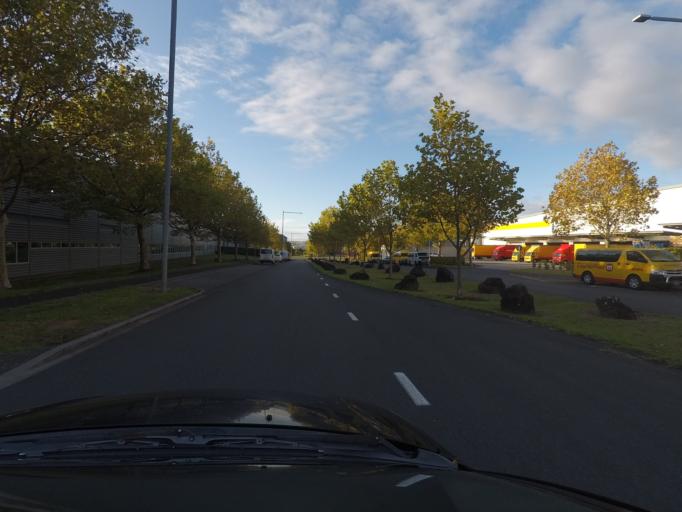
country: NZ
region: Auckland
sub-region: Auckland
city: Manukau City
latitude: -36.9408
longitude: 174.8753
